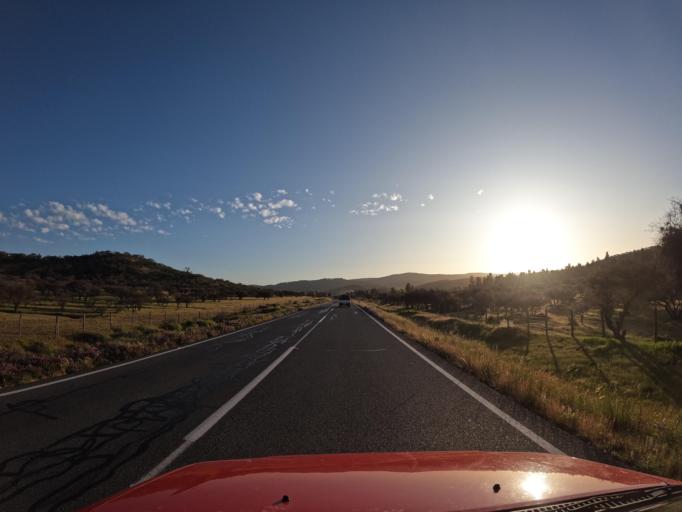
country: CL
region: O'Higgins
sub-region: Provincia de Colchagua
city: Santa Cruz
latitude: -34.3135
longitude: -71.7404
